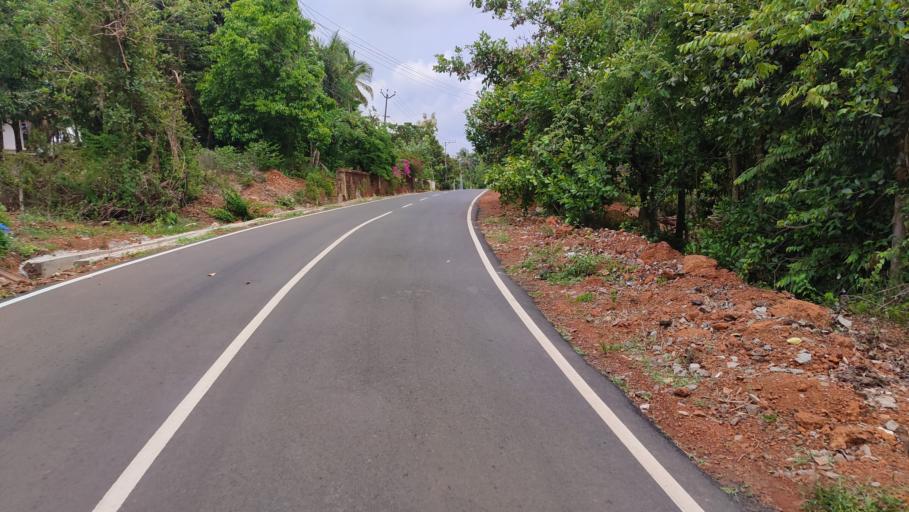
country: IN
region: Kerala
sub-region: Kasaragod District
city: Kannangad
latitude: 12.3194
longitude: 75.1159
